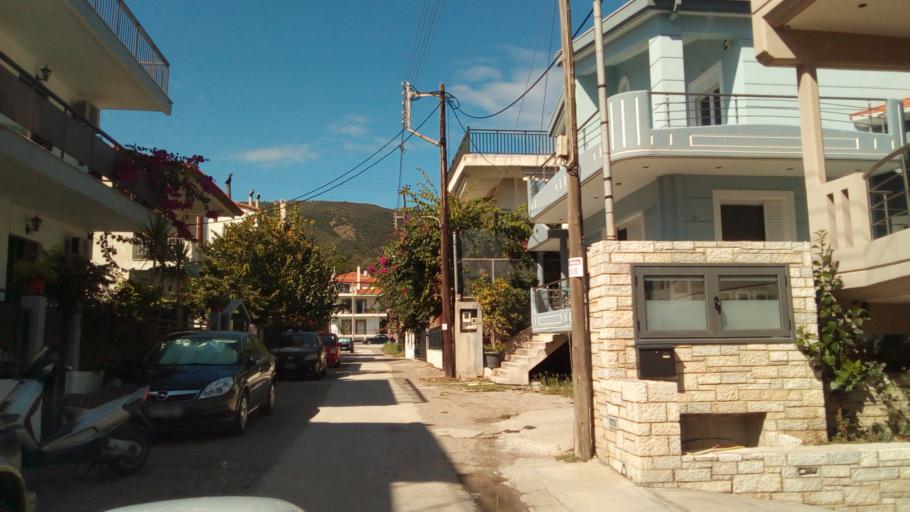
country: GR
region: West Greece
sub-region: Nomos Aitolias kai Akarnanias
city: Antirrio
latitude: 38.3671
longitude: 21.7806
